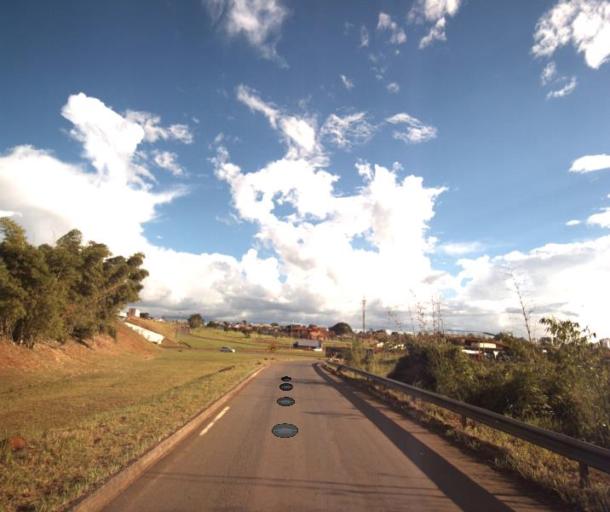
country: BR
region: Goias
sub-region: Anapolis
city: Anapolis
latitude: -16.3245
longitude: -48.9225
